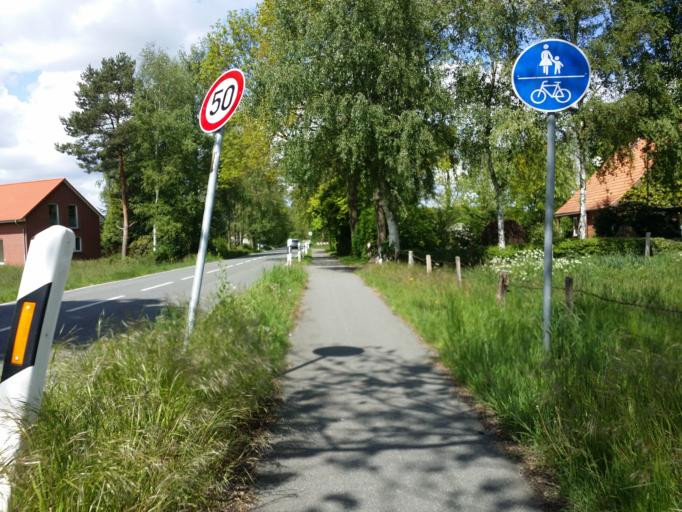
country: DE
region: Lower Saxony
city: Stuhr
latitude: 53.0077
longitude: 8.7407
